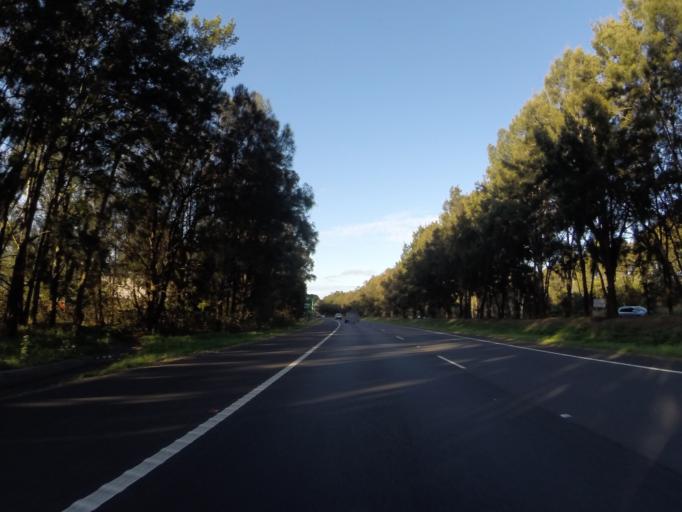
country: AU
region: New South Wales
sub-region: Wollongong
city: Berkeley
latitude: -34.4637
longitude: 150.8500
